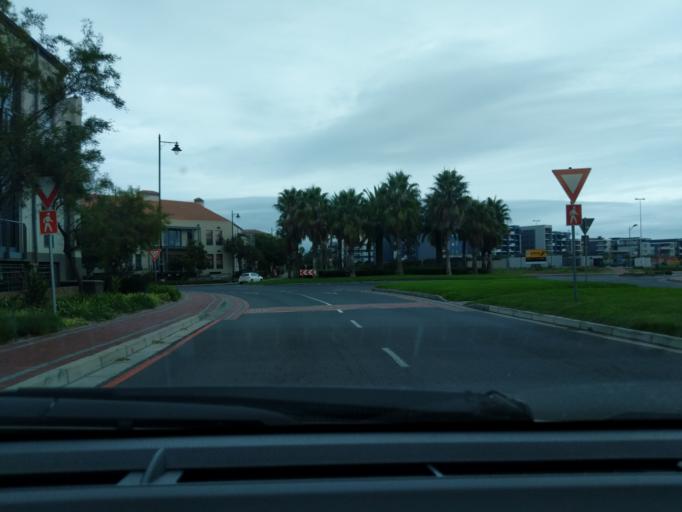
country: ZA
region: Western Cape
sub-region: City of Cape Town
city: Sunset Beach
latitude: -33.8835
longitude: 18.5216
